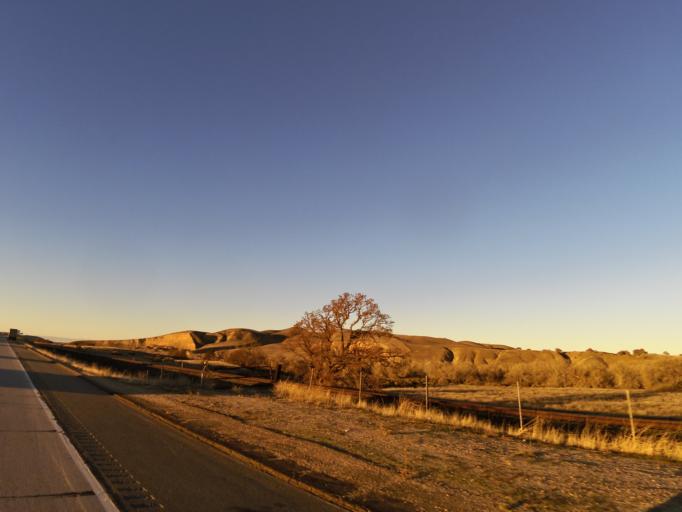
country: US
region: California
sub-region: San Luis Obispo County
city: San Miguel
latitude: 35.7889
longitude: -120.7298
